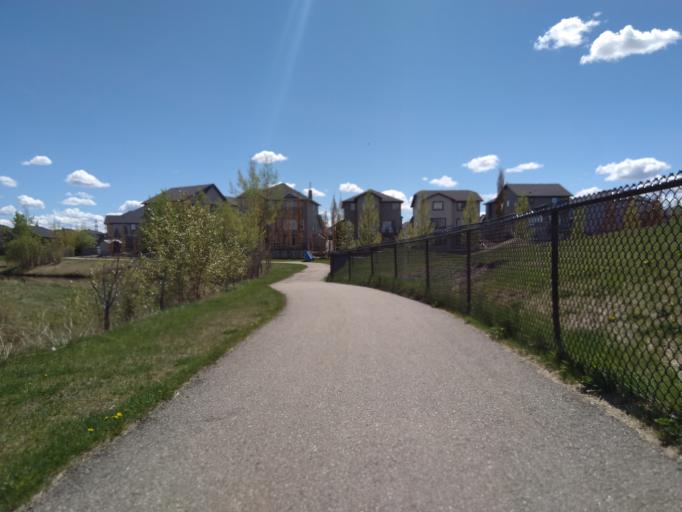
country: CA
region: Alberta
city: Chestermere
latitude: 51.0308
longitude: -113.8377
